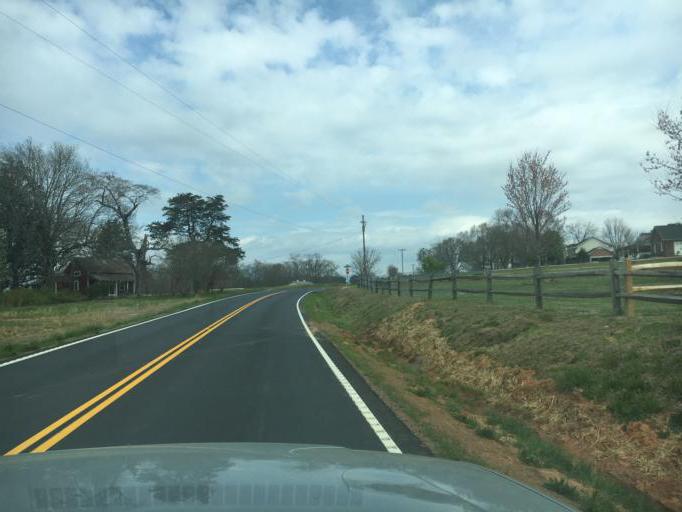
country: US
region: South Carolina
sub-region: Spartanburg County
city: Landrum
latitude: 35.0980
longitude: -82.2061
